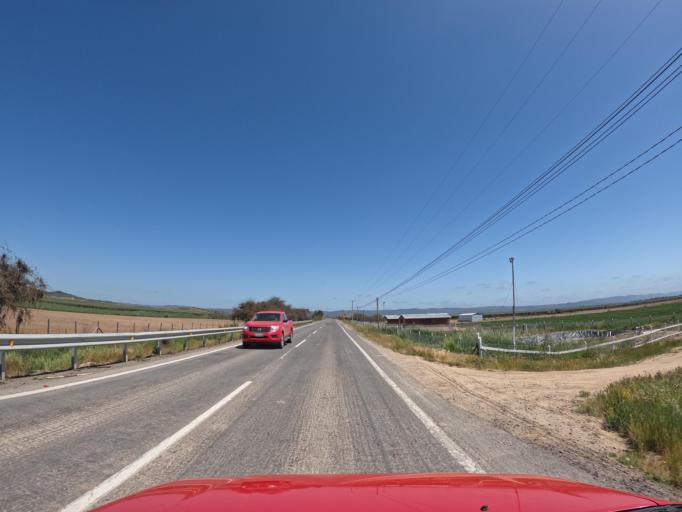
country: CL
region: O'Higgins
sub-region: Provincia de Colchagua
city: Santa Cruz
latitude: -34.7351
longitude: -71.6985
